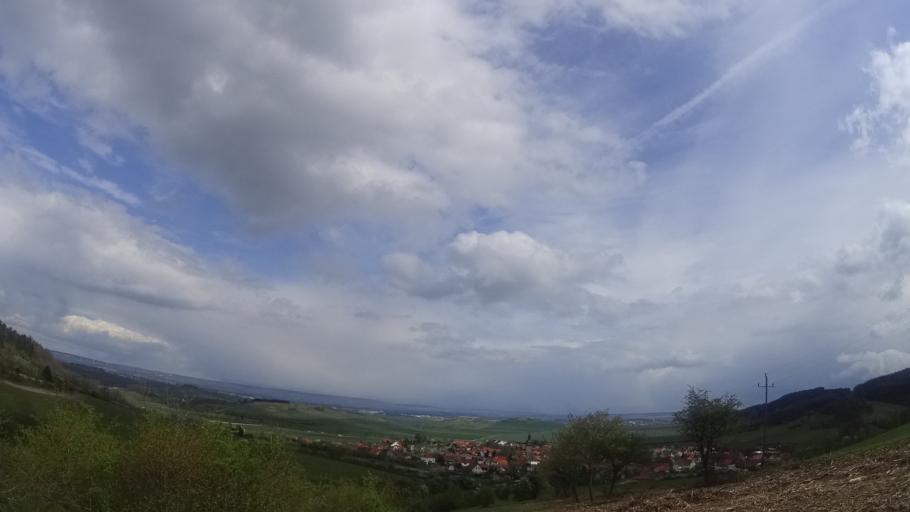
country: DE
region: Thuringia
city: Apfelstadt
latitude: 50.8534
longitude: 10.8736
